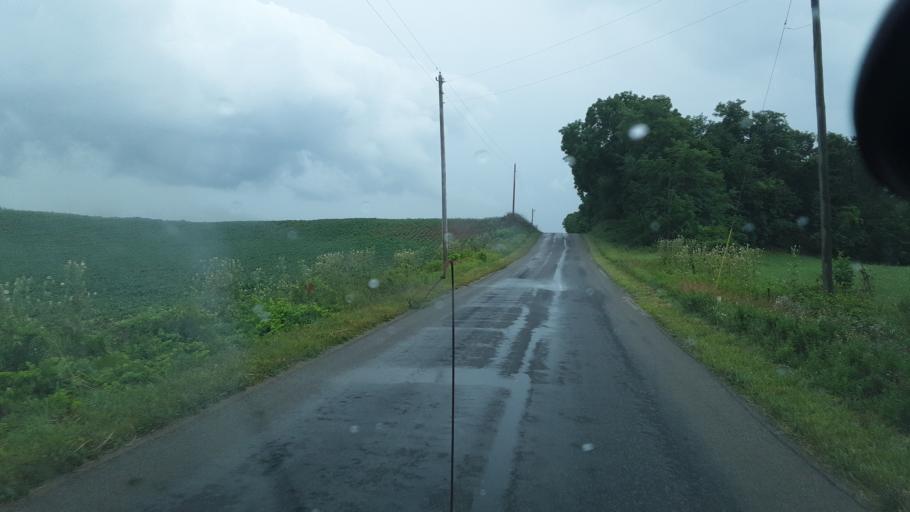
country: US
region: Indiana
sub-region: Steuben County
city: Hamilton
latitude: 41.5554
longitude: -84.8553
